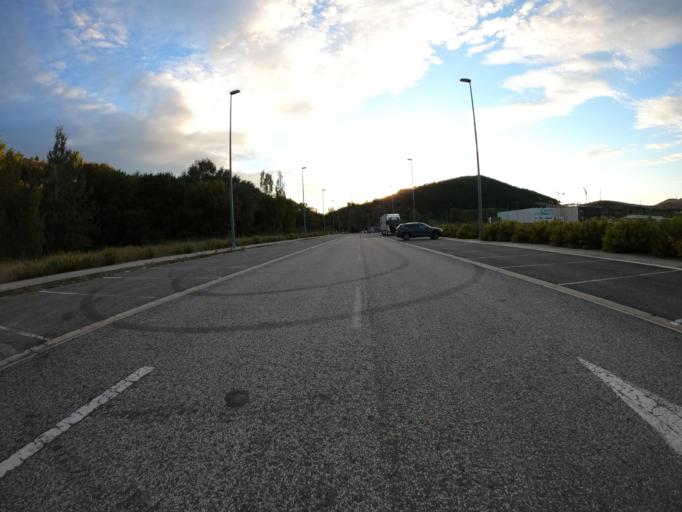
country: ES
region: Navarre
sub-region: Provincia de Navarra
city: Egues-Uharte
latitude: 42.8348
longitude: -1.5835
